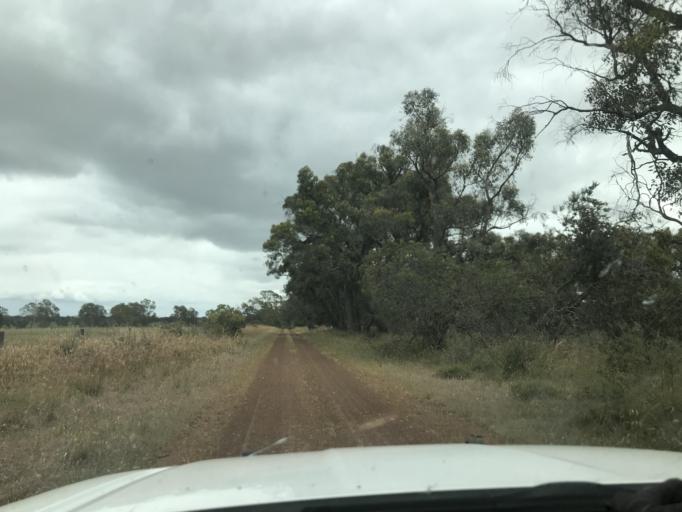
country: AU
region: South Australia
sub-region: Wattle Range
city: Penola
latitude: -37.0981
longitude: 141.2717
